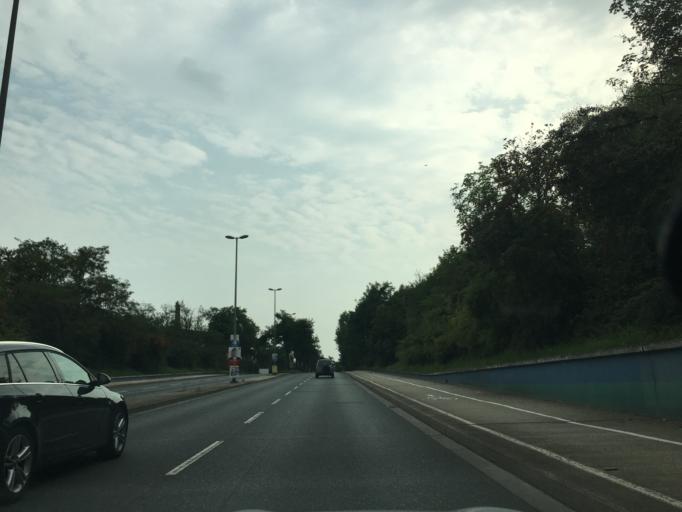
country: DE
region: Hesse
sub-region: Regierungsbezirk Darmstadt
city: Russelsheim
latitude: 49.9941
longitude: 8.4245
